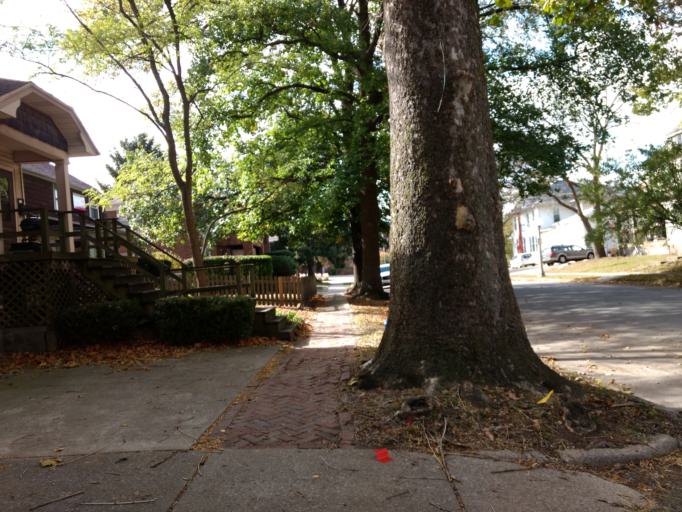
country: US
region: Illinois
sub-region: Champaign County
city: Urbana
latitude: 40.1082
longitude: -88.2181
